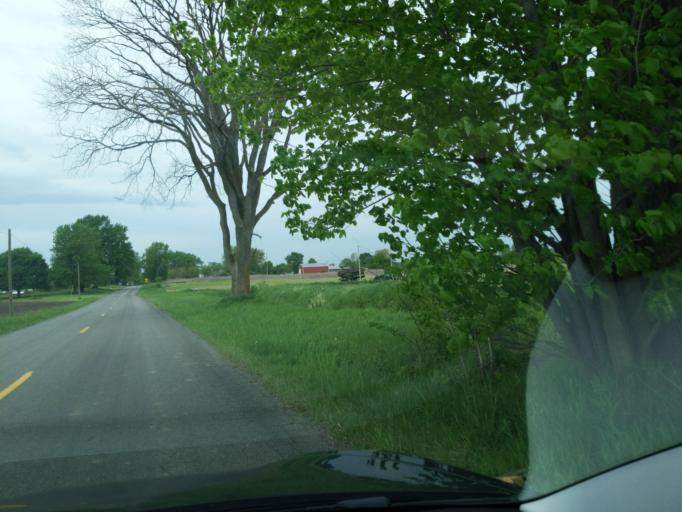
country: US
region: Michigan
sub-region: Ingham County
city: Stockbridge
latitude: 42.4285
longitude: -84.2142
